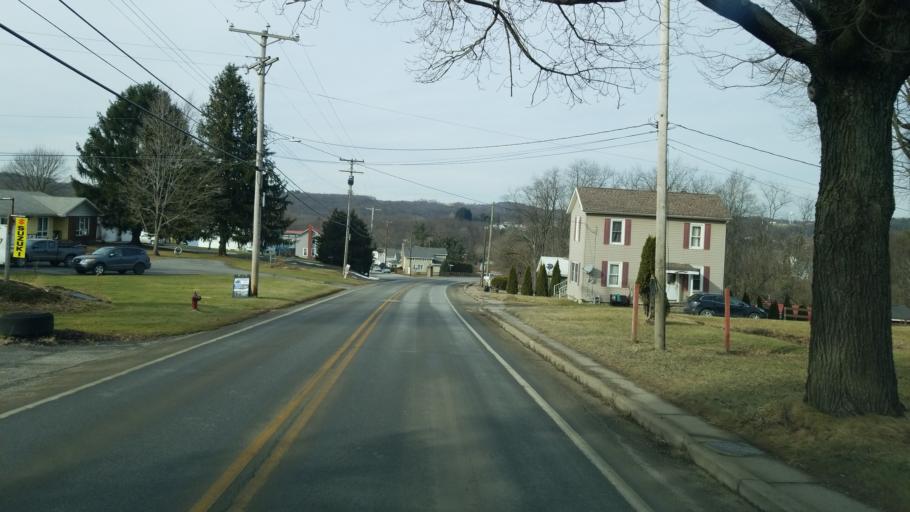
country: US
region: Pennsylvania
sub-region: Jefferson County
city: Punxsutawney
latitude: 40.9372
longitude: -78.9920
